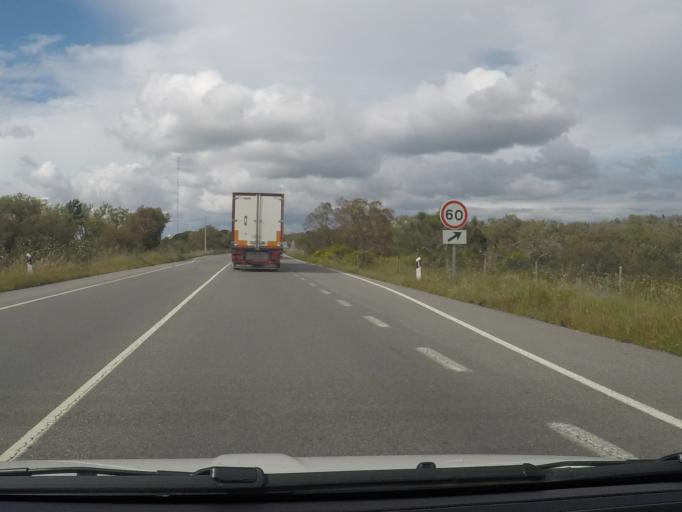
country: PT
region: Setubal
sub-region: Grandola
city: Grandola
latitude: 38.1532
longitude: -8.6495
